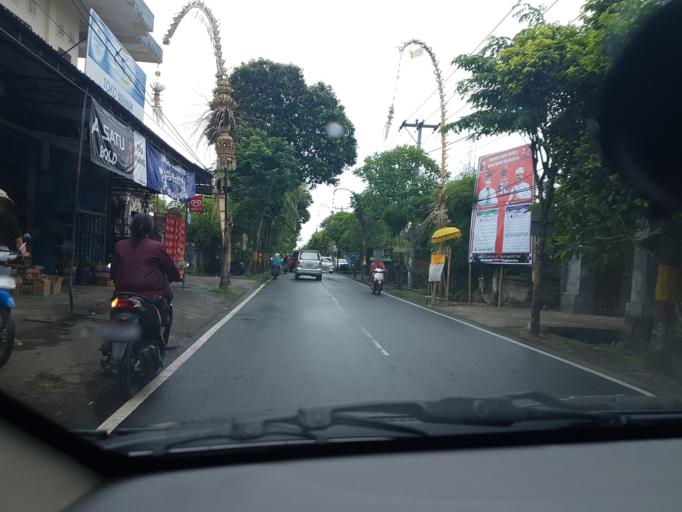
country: ID
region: Bali
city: Banjar Sedang
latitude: -8.5766
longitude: 115.2385
